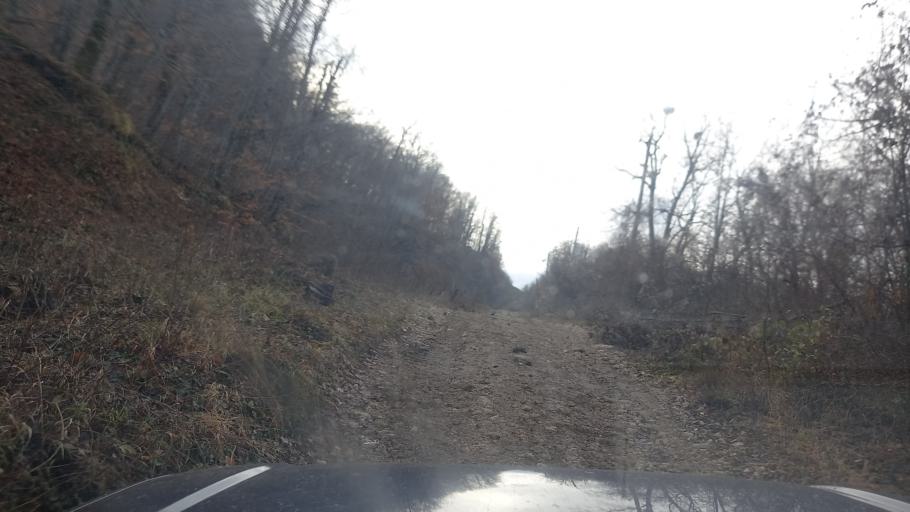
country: RU
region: Krasnodarskiy
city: Neftegorsk
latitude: 44.2070
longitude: 39.7091
